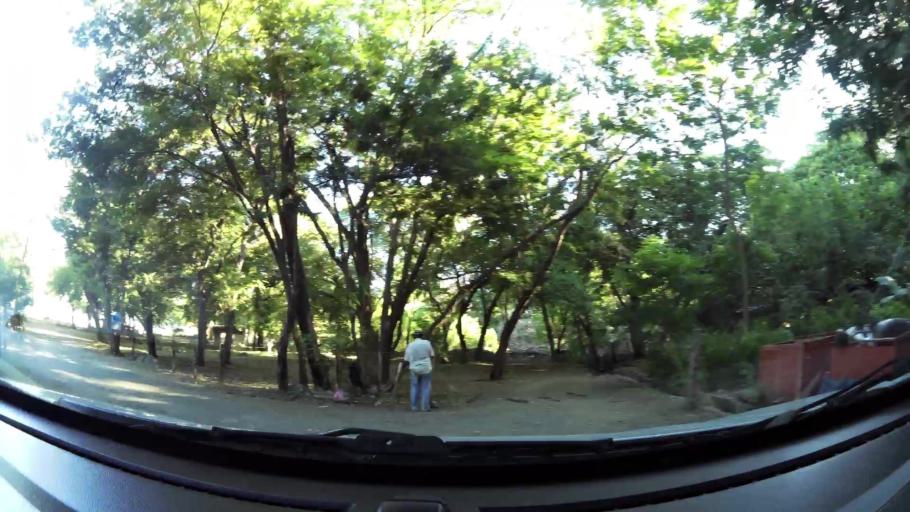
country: CR
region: Guanacaste
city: Sardinal
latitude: 10.5714
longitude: -85.6802
